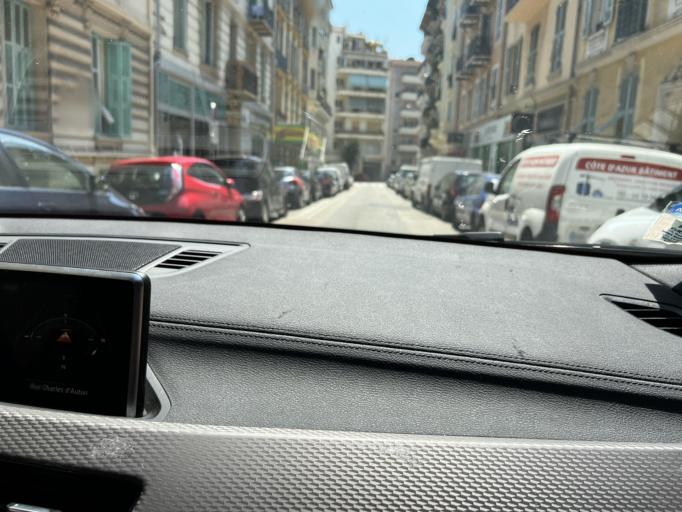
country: FR
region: Provence-Alpes-Cote d'Azur
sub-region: Departement des Alpes-Maritimes
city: Nice
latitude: 43.7080
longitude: 7.2615
